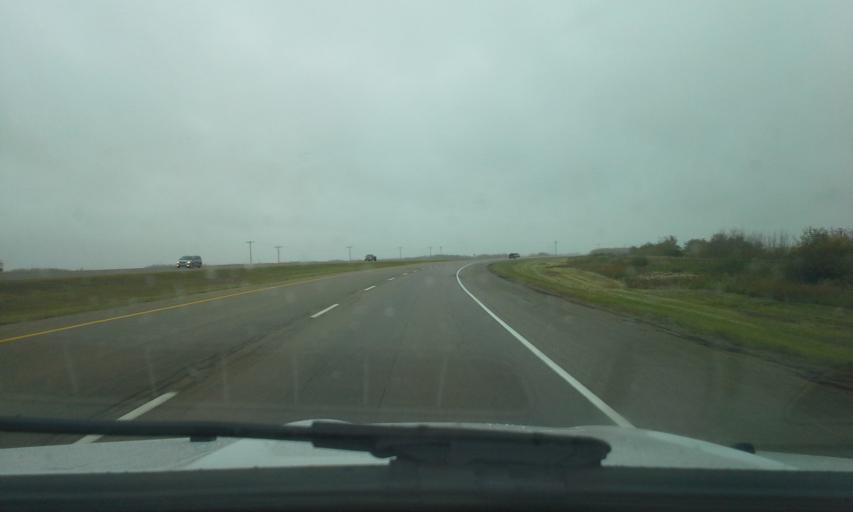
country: CA
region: Saskatchewan
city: Lloydminster
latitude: 53.2278
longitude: -109.8265
